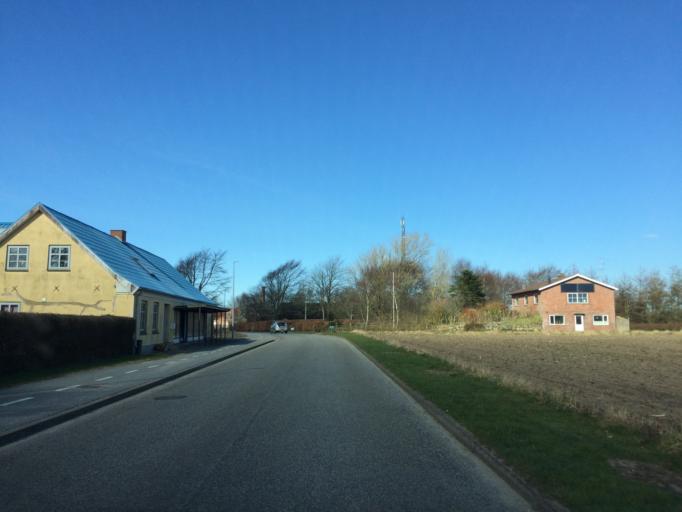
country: DK
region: South Denmark
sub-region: Varde Kommune
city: Oksbol
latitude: 55.7328
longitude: 8.2678
